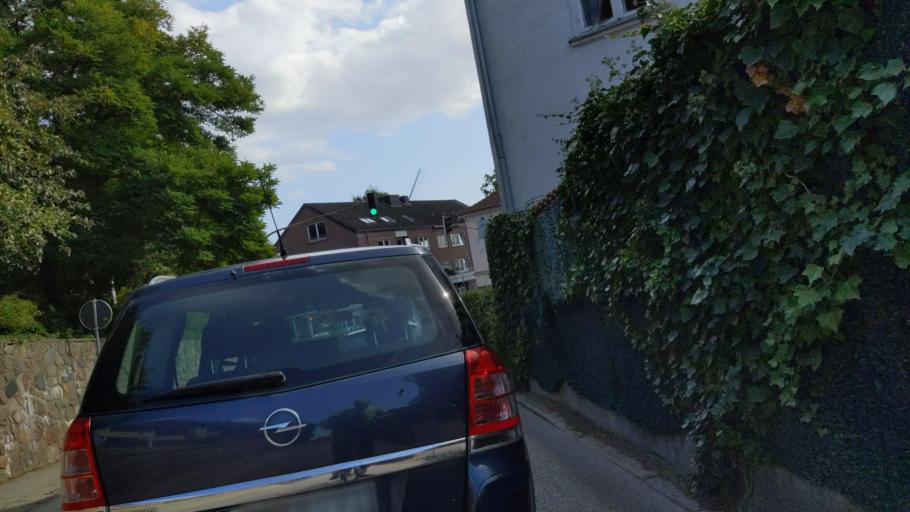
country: DE
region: Schleswig-Holstein
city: Eutin
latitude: 54.1377
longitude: 10.6083
